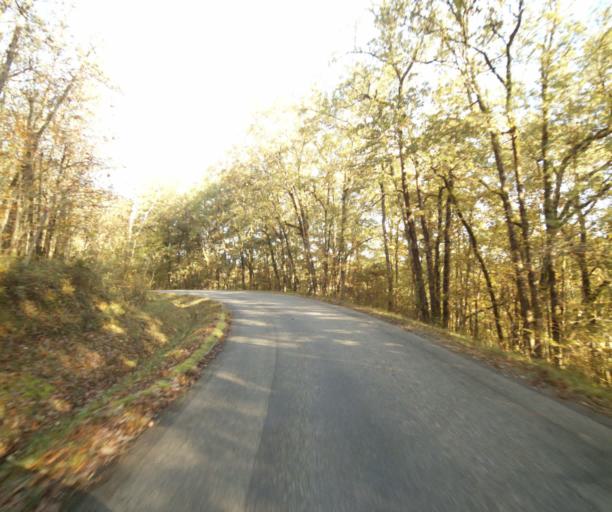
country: FR
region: Midi-Pyrenees
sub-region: Departement de la Haute-Garonne
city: Villemur-sur-Tarn
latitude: 43.8911
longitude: 1.4983
